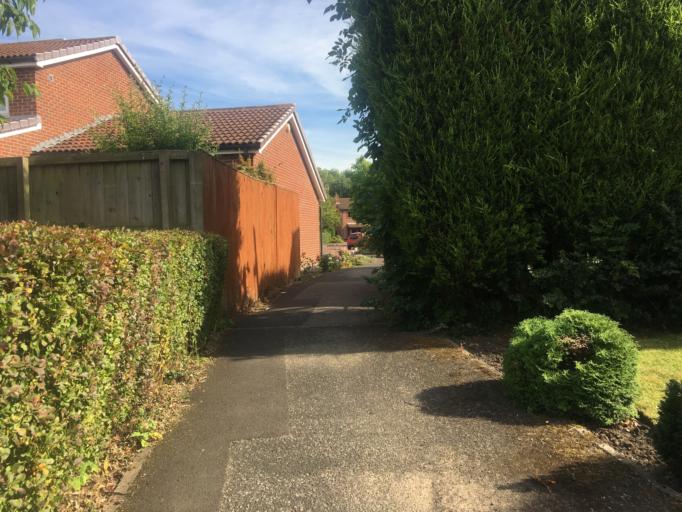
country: GB
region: England
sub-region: County Durham
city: Chester-le-Street
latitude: 54.8770
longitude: -1.5544
